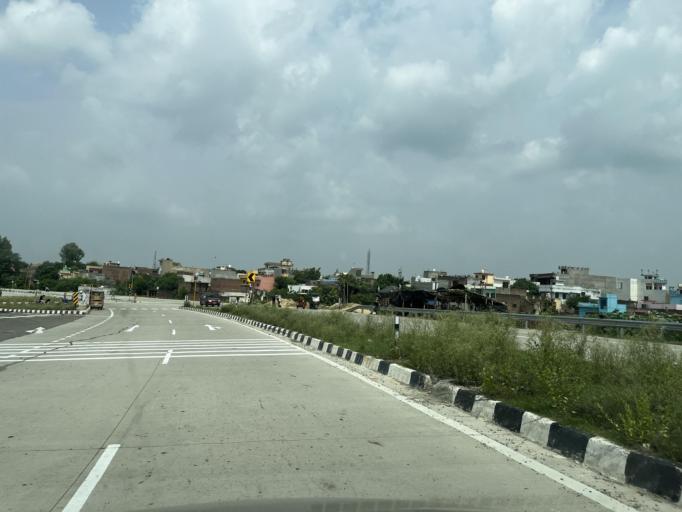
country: IN
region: Uttar Pradesh
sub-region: Bijnor
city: Sherkot
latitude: 29.3268
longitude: 78.5683
